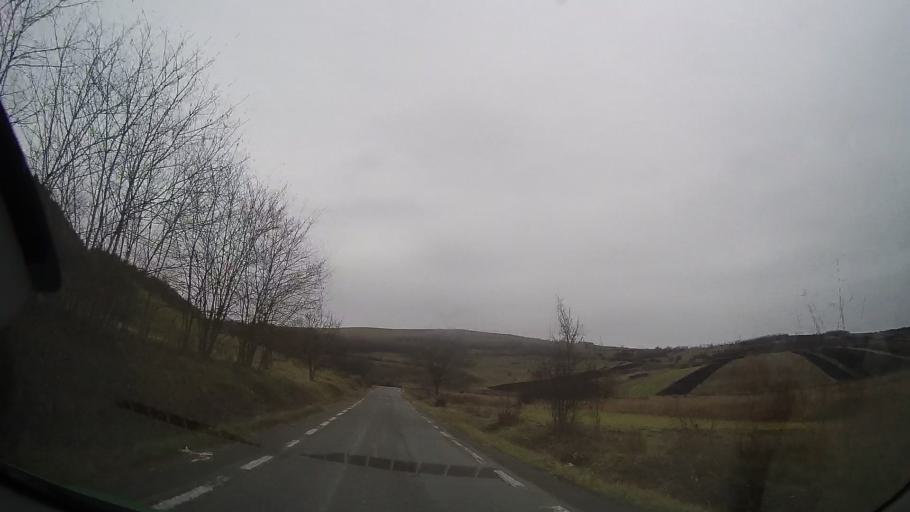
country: RO
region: Mures
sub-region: Comuna Bala
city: Bala
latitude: 46.7153
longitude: 24.5249
